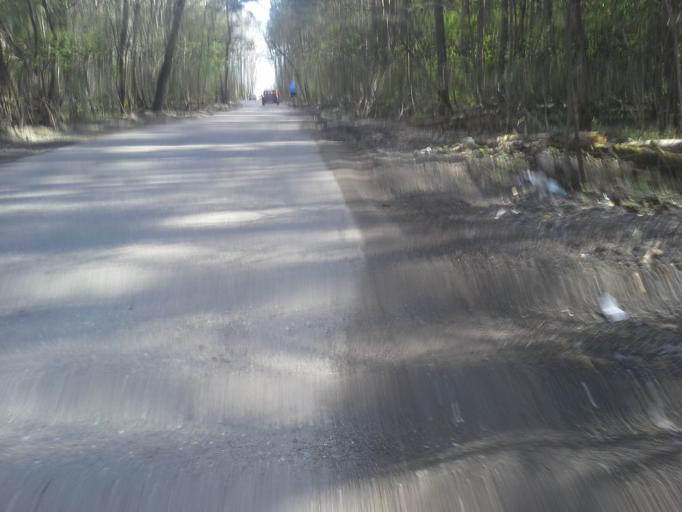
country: RU
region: Moskovskaya
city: Dubrovitsy
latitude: 55.4645
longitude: 37.4412
